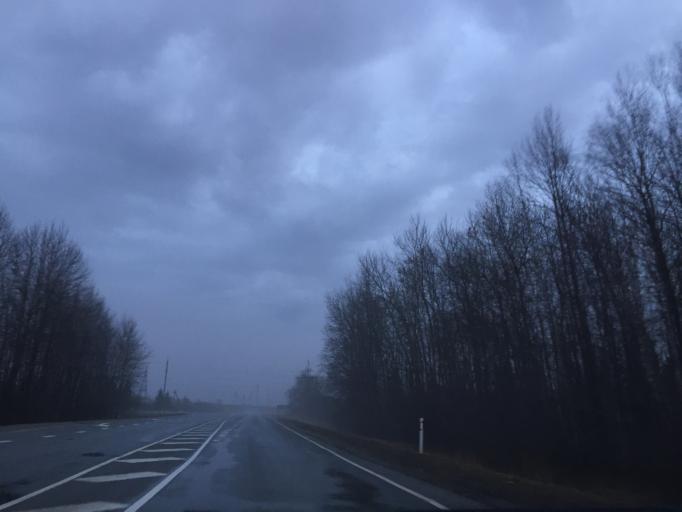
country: EE
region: Laeaene
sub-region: Lihula vald
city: Lihula
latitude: 58.6818
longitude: 23.8129
